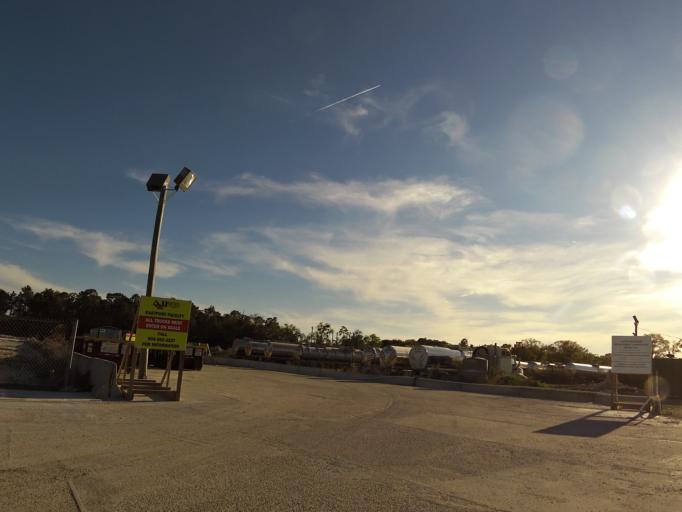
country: US
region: Florida
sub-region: Duval County
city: Jacksonville
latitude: 30.4424
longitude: -81.6131
